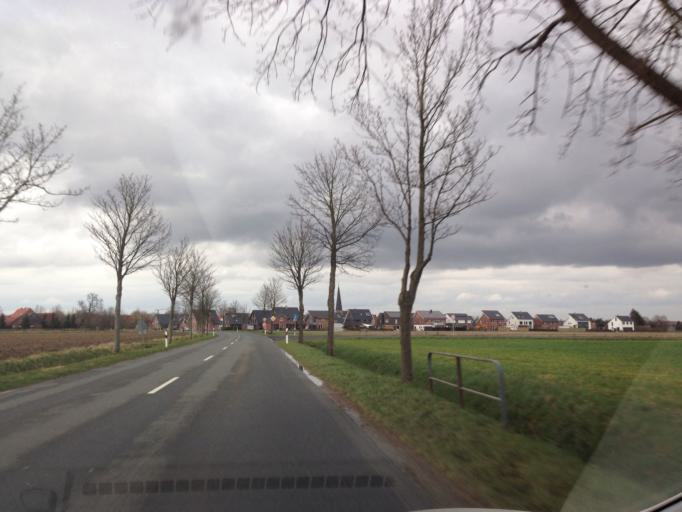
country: DE
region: North Rhine-Westphalia
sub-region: Regierungsbezirk Munster
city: Senden
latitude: 51.8159
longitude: 7.5391
